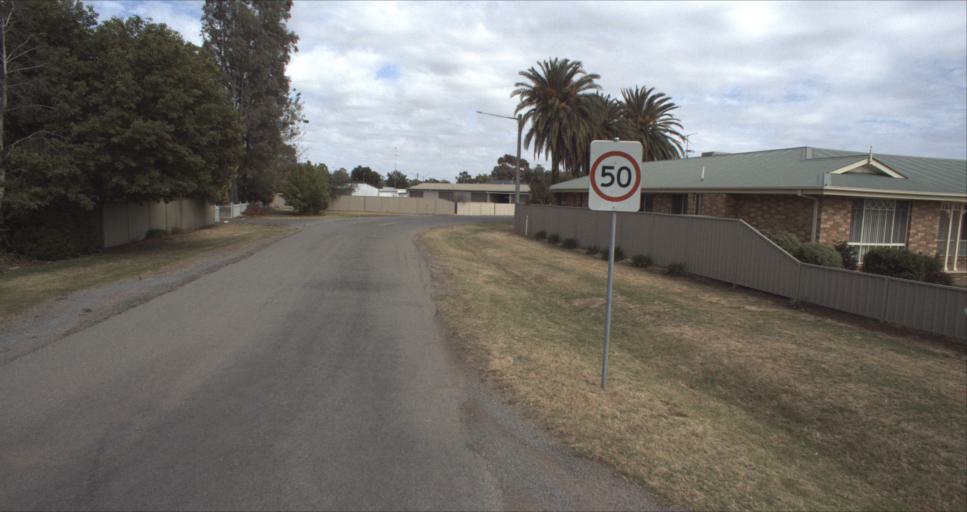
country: AU
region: New South Wales
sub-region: Leeton
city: Leeton
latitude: -34.5593
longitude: 146.4156
